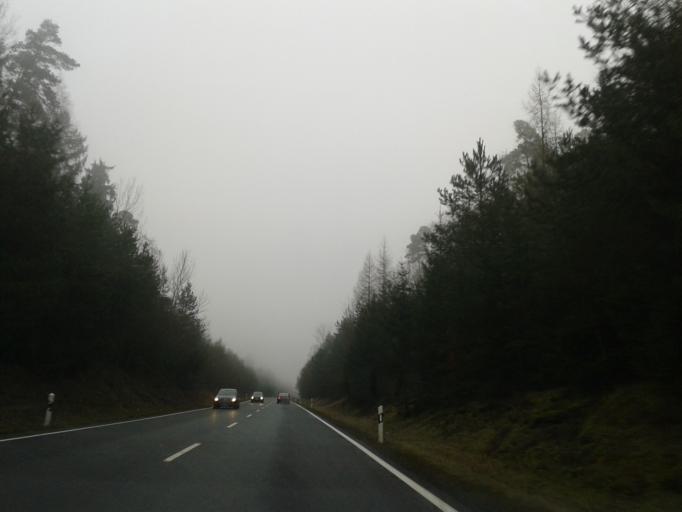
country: DE
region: Bavaria
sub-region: Regierungsbezirk Unterfranken
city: Hofheim in Unterfranken
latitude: 50.1300
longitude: 10.5804
